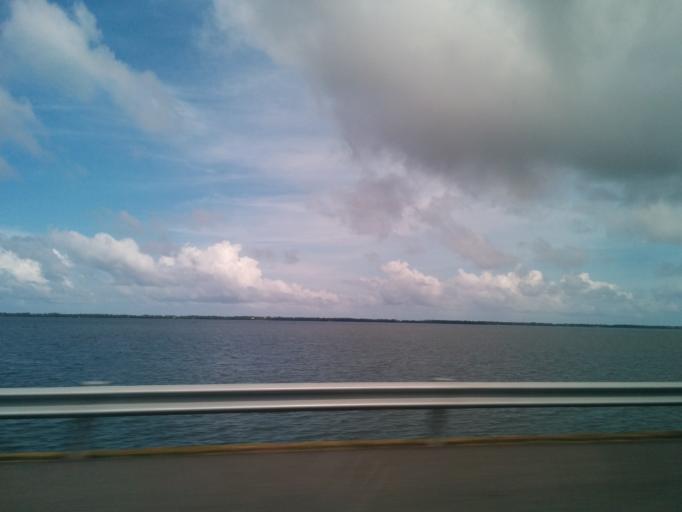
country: LK
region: Western
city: Katunayaka
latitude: 7.1406
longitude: 79.8676
